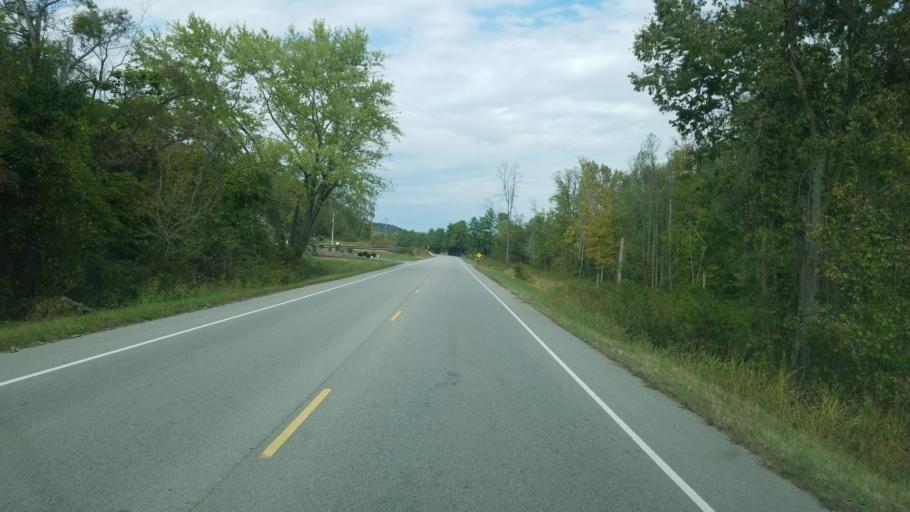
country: US
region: West Virginia
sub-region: Mason County
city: Point Pleasant
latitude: 38.8709
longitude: -82.1427
